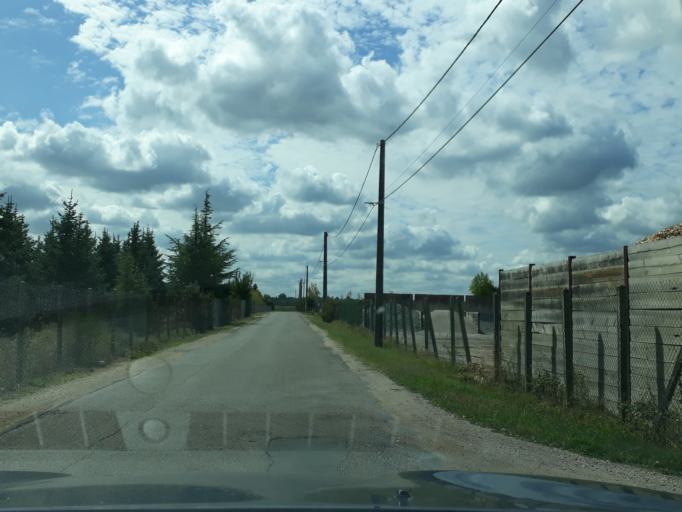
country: FR
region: Centre
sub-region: Departement du Loiret
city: Saint-Cyr-en-Val
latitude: 47.8452
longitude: 1.9732
